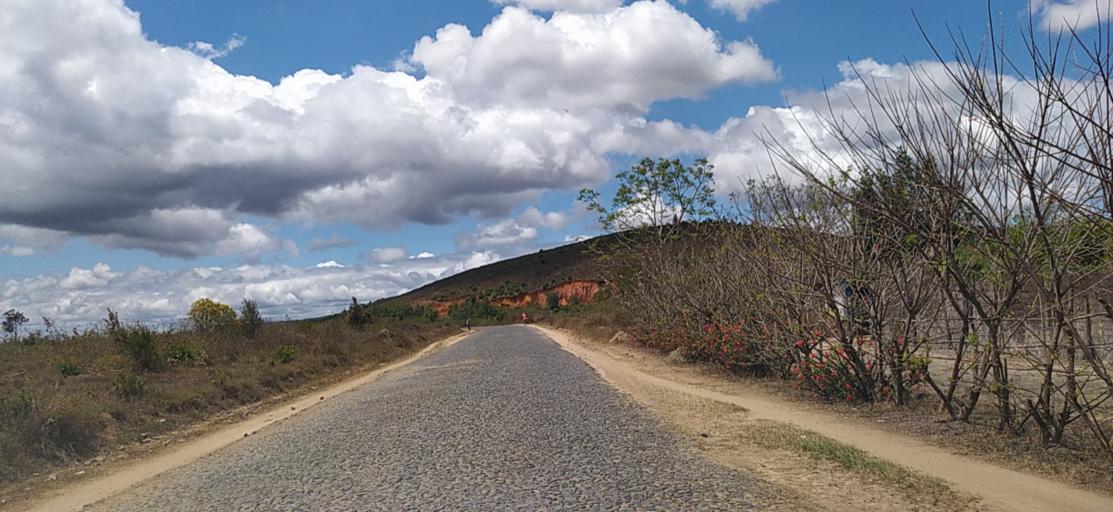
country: MG
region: Alaotra Mangoro
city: Moramanga
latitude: -18.7593
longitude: 48.2578
